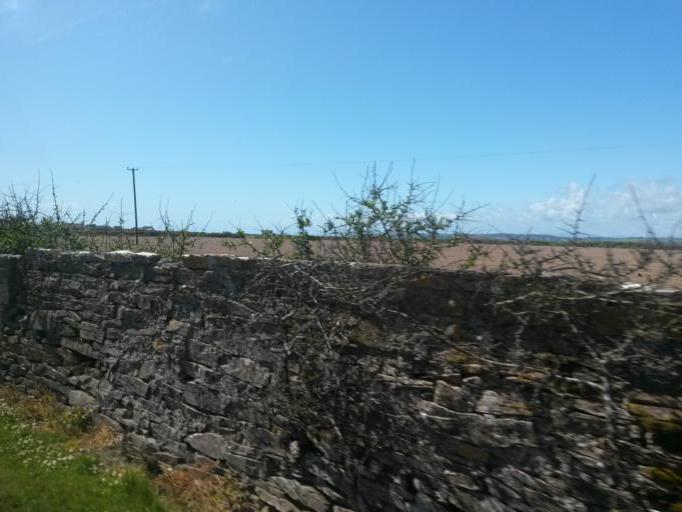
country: IE
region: Munster
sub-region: Waterford
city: Dunmore East
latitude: 52.1398
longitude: -6.9140
